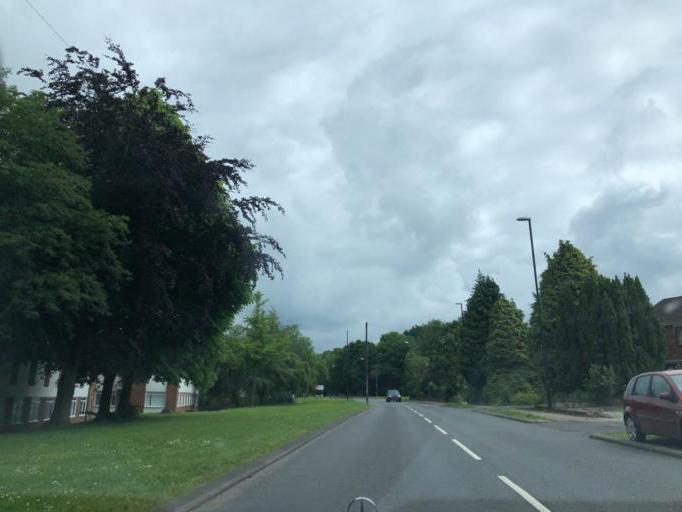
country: GB
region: England
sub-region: Warwickshire
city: Kenilworth
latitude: 52.3927
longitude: -1.5944
